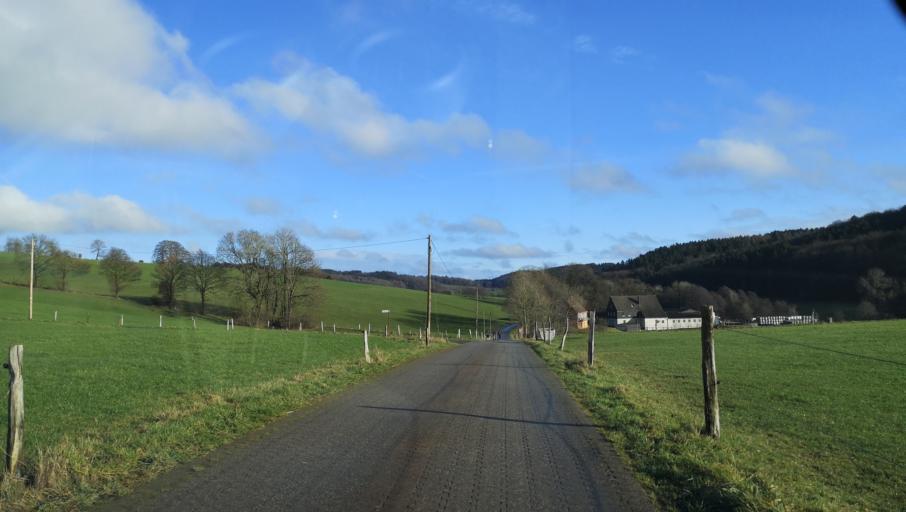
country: DE
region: North Rhine-Westphalia
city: Radevormwald
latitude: 51.1790
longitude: 7.4072
